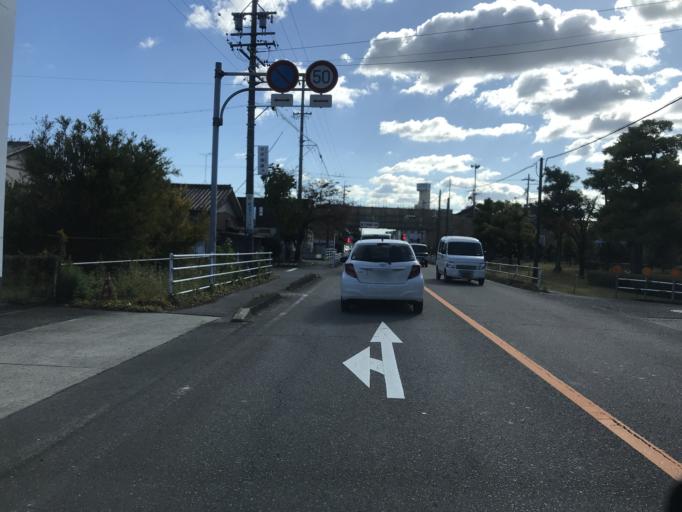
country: JP
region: Aichi
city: Nagoya-shi
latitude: 35.2091
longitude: 136.8543
